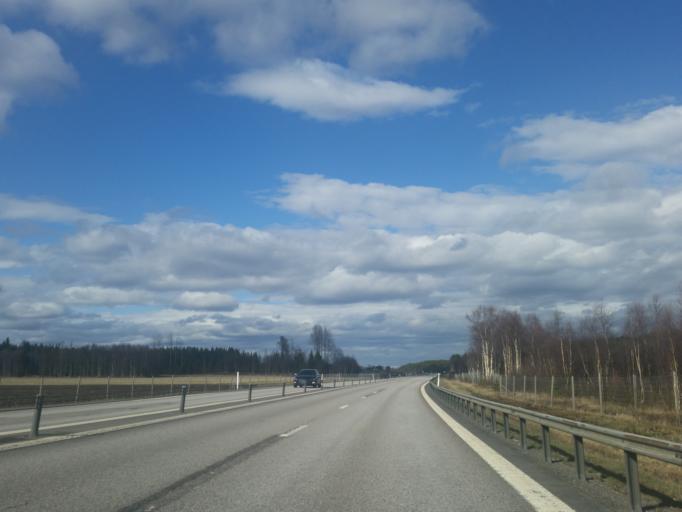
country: SE
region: Vaesterbotten
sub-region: Robertsfors Kommun
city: Robertsfors
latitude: 64.1445
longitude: 20.8987
